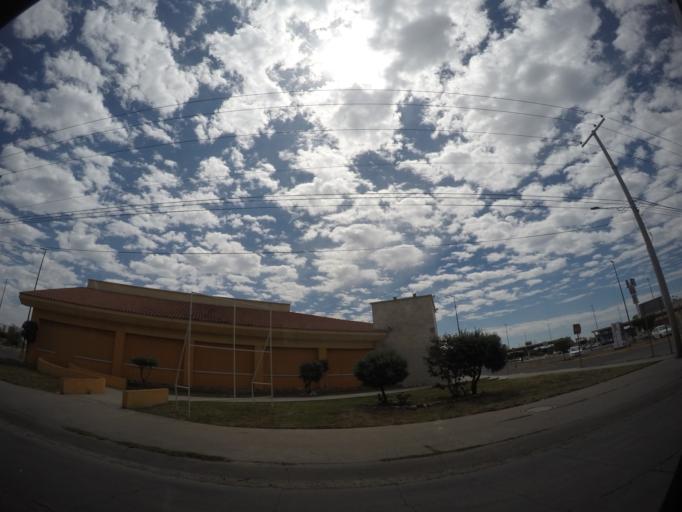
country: MX
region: Guanajuato
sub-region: Leon
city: San Jose de Duran (Los Troncoso)
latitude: 21.0880
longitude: -101.6654
